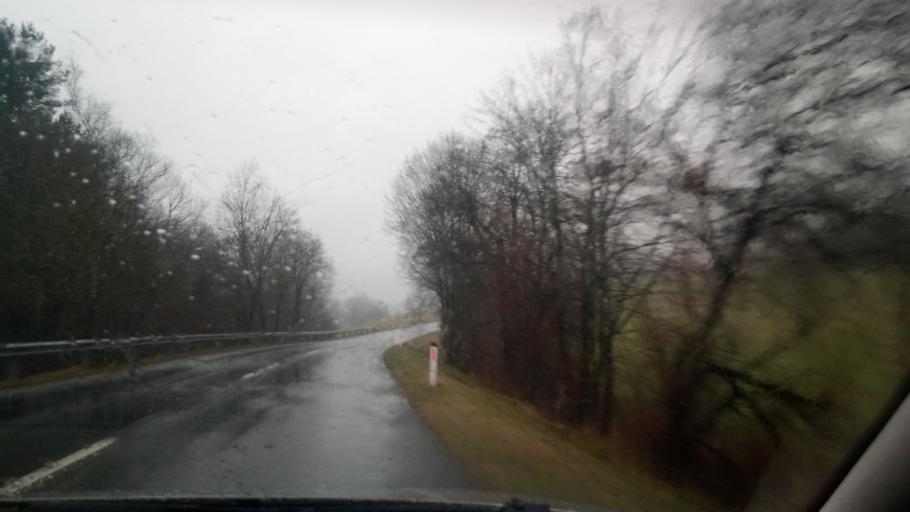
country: AT
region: Carinthia
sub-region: Politischer Bezirk Klagenfurt Land
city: Keutschach am See
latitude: 46.5890
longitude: 14.1783
